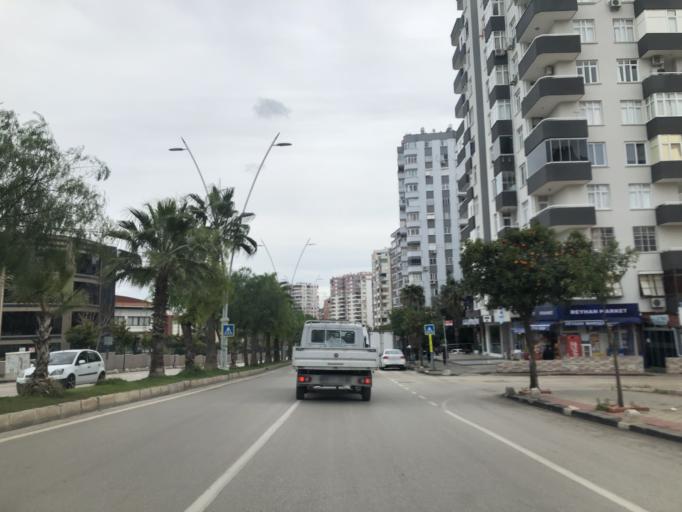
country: TR
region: Adana
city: Adana
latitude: 37.0540
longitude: 35.2890
